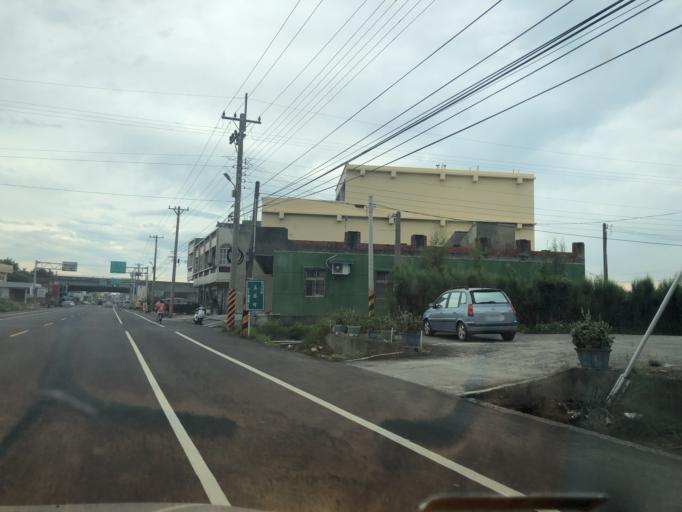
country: TW
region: Taiwan
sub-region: Chiayi
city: Taibao
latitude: 23.7108
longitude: 120.2010
